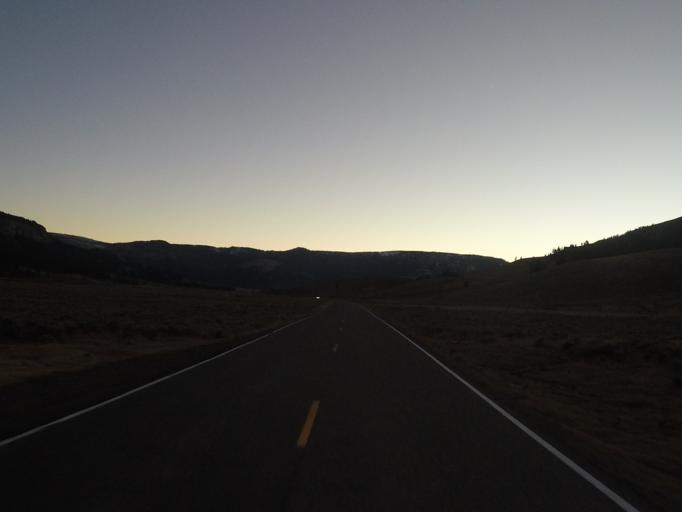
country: US
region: Montana
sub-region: Park County
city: Livingston
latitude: 44.8899
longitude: -110.1387
